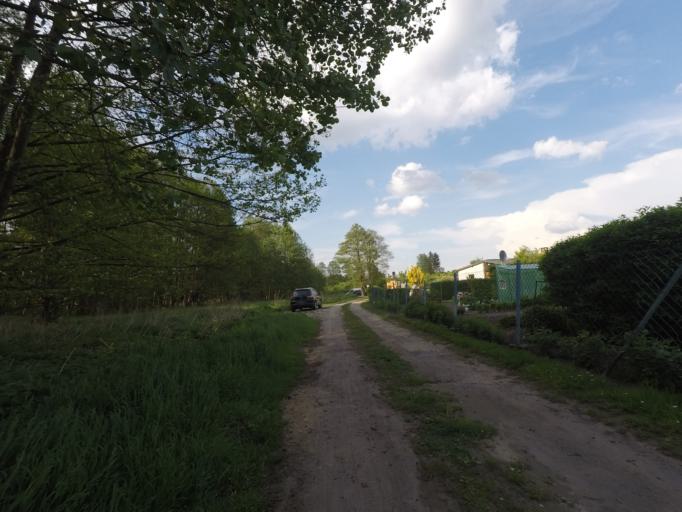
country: DE
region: Brandenburg
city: Melchow
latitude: 52.8437
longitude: 13.7128
